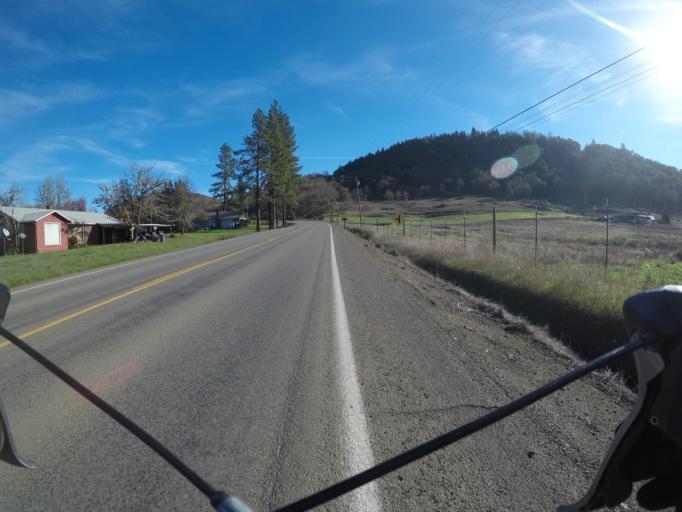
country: US
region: Oregon
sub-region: Douglas County
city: Winston
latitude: 43.1860
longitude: -123.4612
